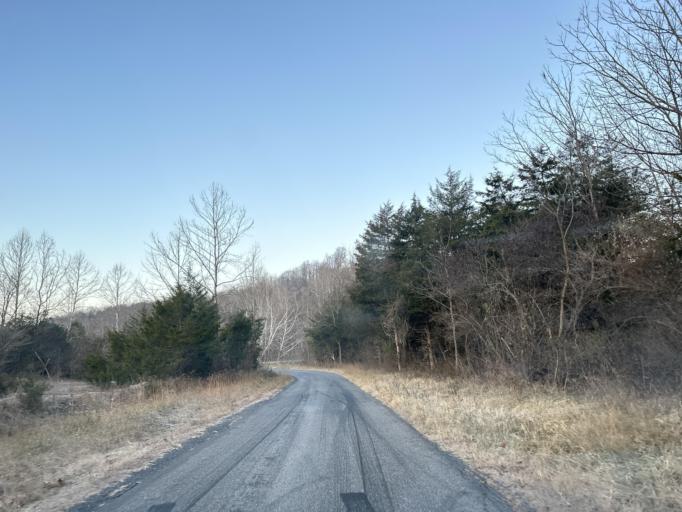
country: US
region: Virginia
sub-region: Rockbridge County
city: East Lexington
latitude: 38.0755
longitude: -79.3734
